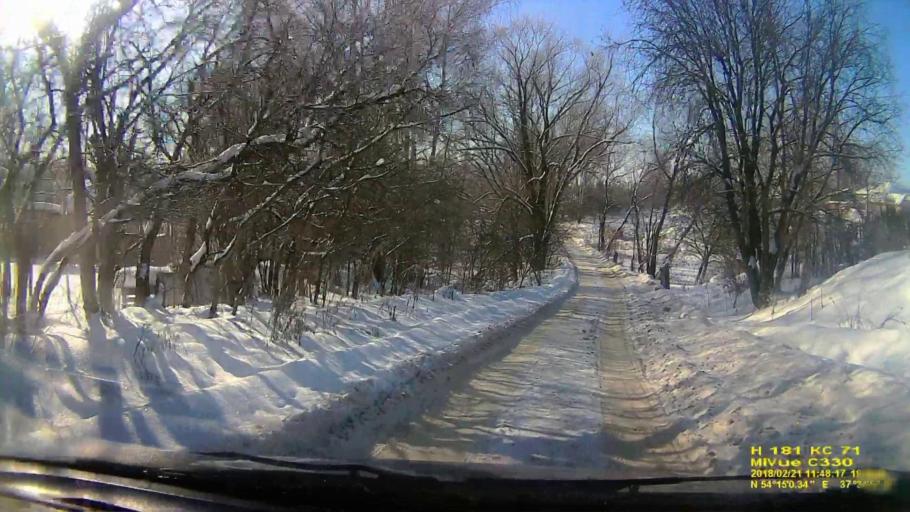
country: RU
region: Tula
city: Gorelki
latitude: 54.2500
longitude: 37.5826
